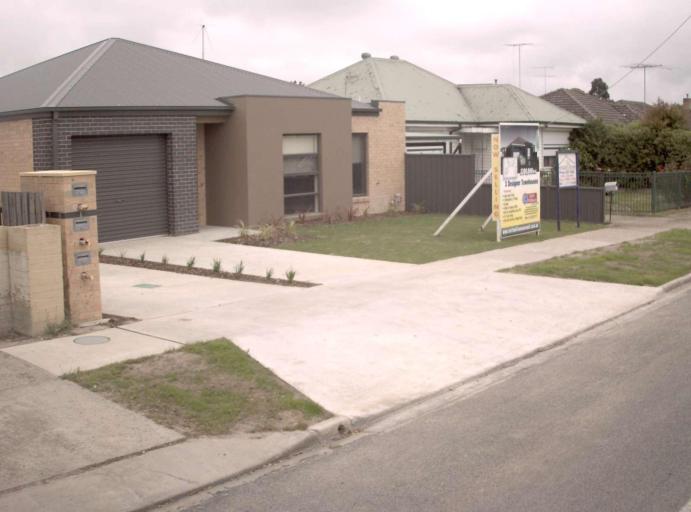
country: AU
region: Victoria
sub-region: Latrobe
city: Morwell
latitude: -38.2369
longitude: 146.4053
